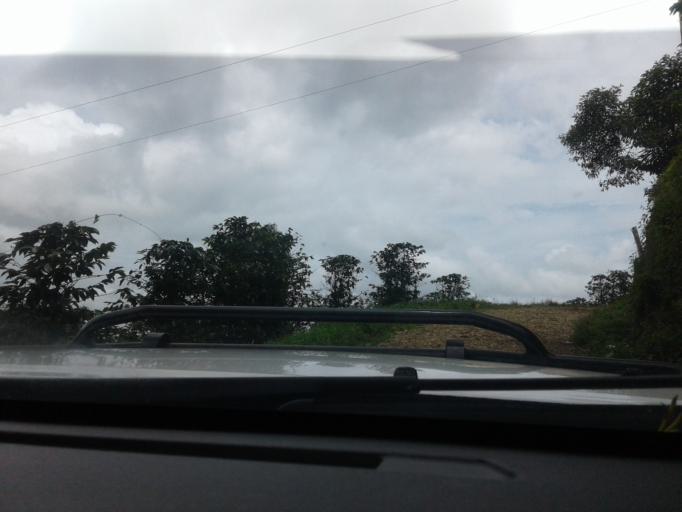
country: NI
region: Matagalpa
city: San Ramon
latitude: 13.0515
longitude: -85.8743
